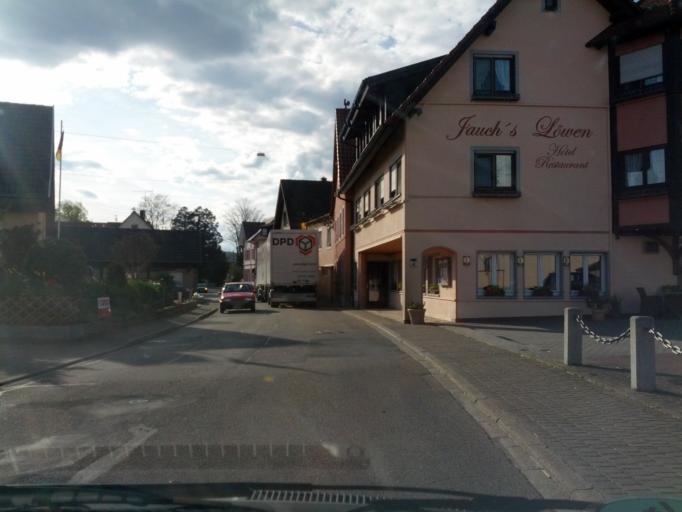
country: DE
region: Baden-Wuerttemberg
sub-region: Freiburg Region
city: Umkirch
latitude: 48.0686
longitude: 7.7717
